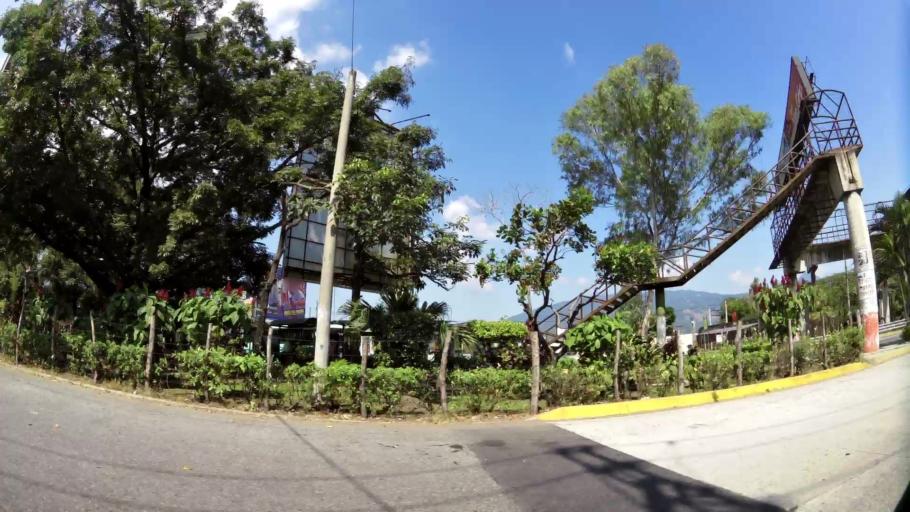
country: SV
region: La Libertad
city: Antiguo Cuscatlan
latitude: 13.6706
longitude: -89.2632
